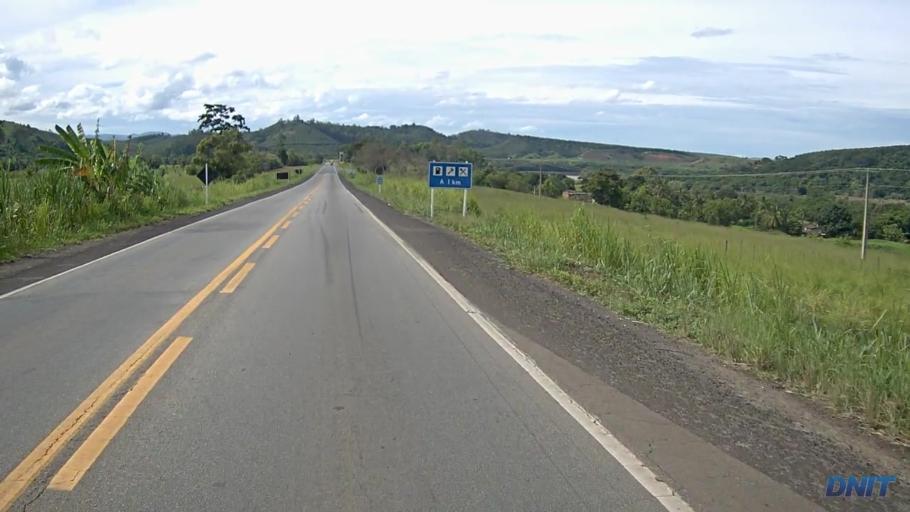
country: BR
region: Minas Gerais
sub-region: Ipaba
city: Ipaba
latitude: -19.2921
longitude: -42.3558
